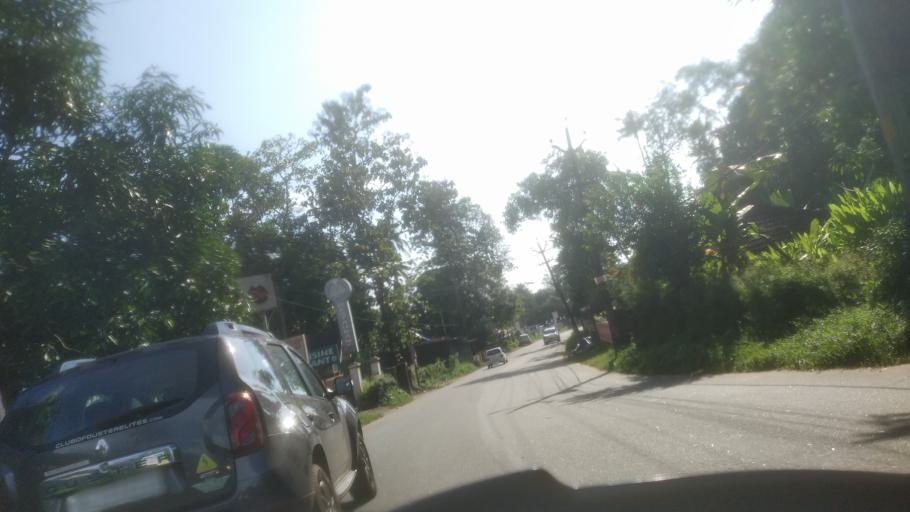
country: IN
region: Kerala
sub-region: Ernakulam
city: Muvattupula
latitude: 9.9879
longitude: 76.5681
